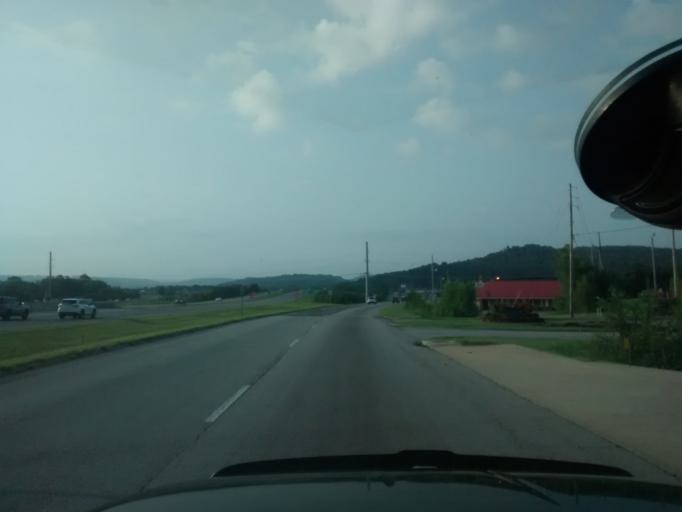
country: US
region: Arkansas
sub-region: Washington County
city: Fayetteville
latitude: 36.0584
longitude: -94.1975
